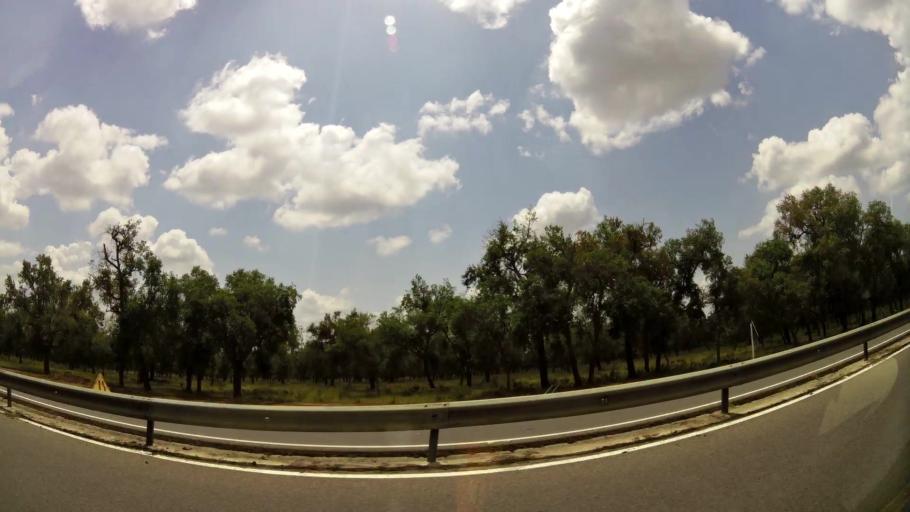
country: MA
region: Rabat-Sale-Zemmour-Zaer
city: Sale
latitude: 34.0194
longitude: -6.5709
